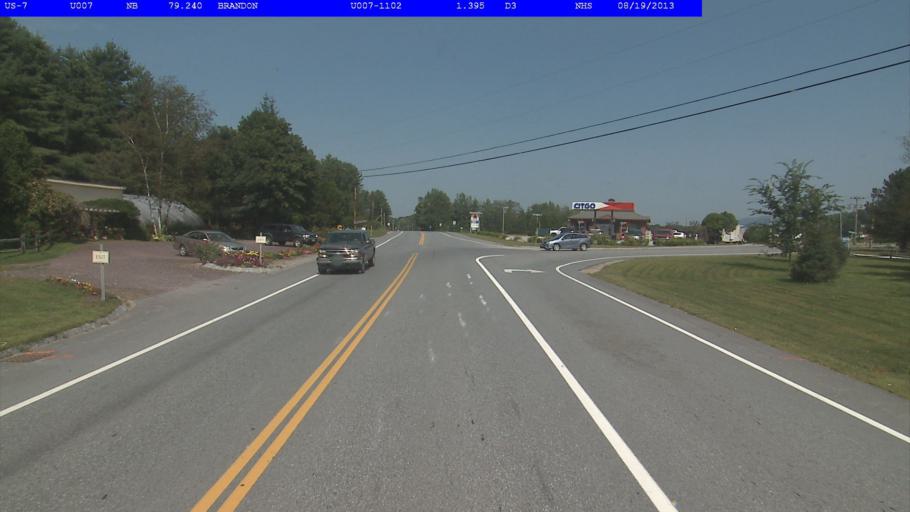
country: US
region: Vermont
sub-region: Rutland County
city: Brandon
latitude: 43.7741
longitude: -73.0532
